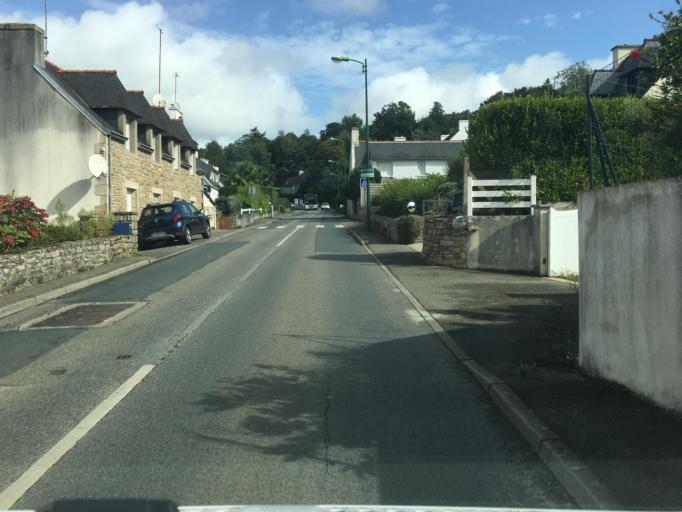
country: FR
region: Brittany
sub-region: Departement du Finistere
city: La Foret-Fouesnant
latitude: 47.9126
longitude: -3.9744
